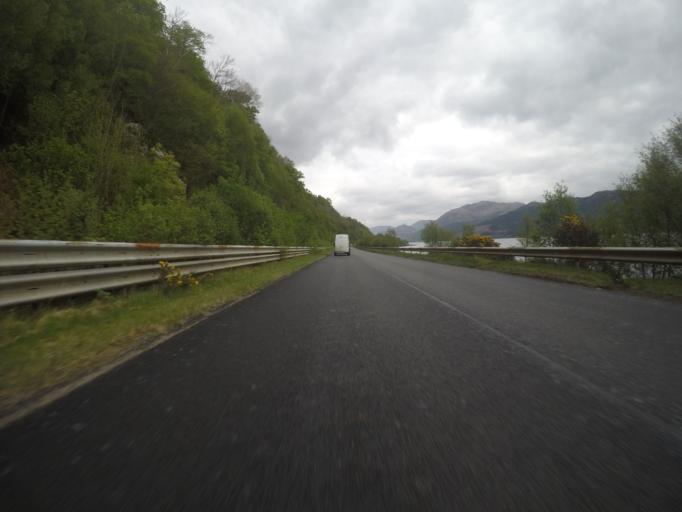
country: GB
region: Scotland
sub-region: Highland
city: Fort William
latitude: 57.2553
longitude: -5.4789
